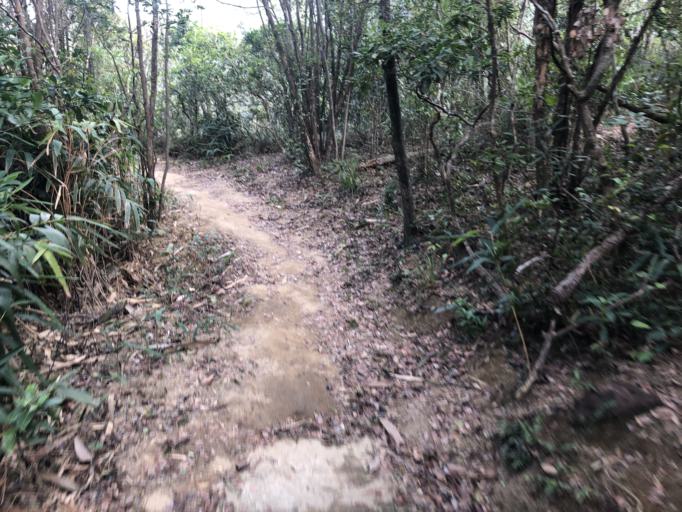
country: HK
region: Wanchai
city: Wan Chai
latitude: 22.2719
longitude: 114.2116
